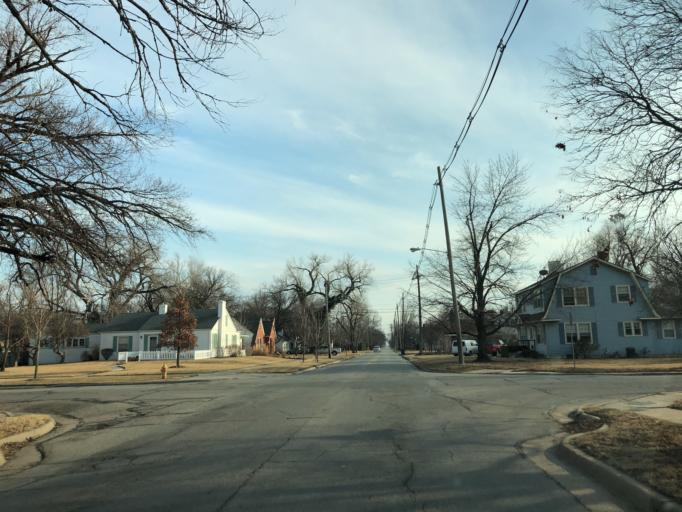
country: US
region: Kansas
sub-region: Reno County
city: Hutchinson
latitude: 38.0792
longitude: -97.9355
